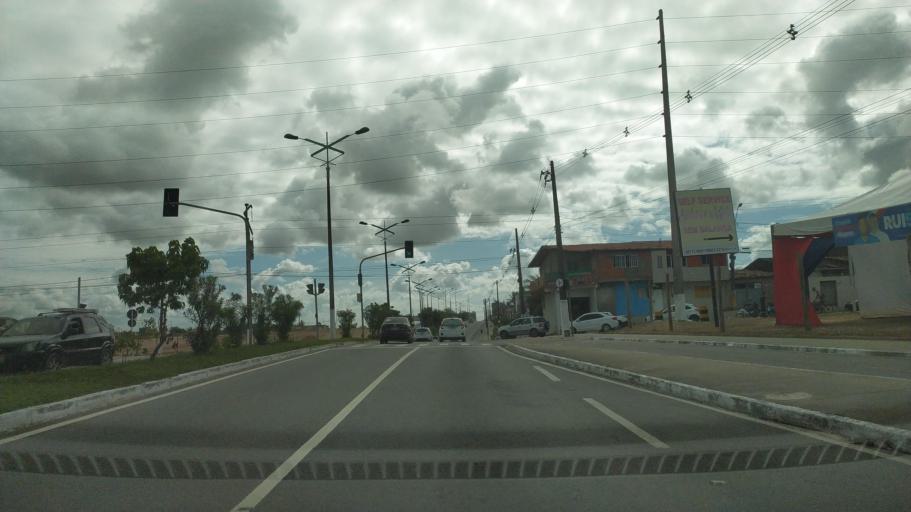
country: BR
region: Alagoas
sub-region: Maceio
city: Maceio
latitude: -9.6228
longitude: -35.7073
